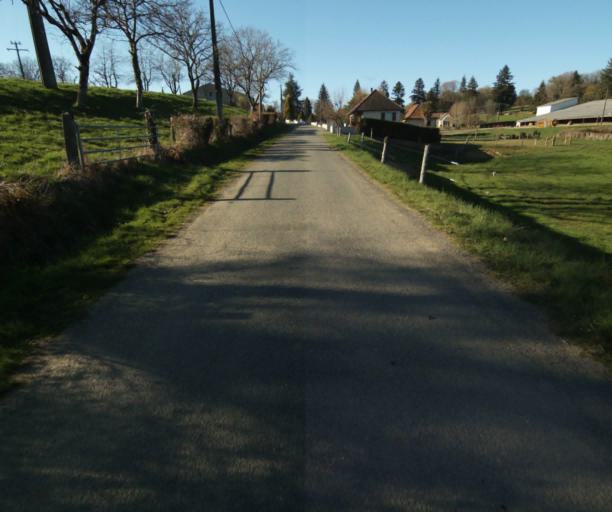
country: FR
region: Limousin
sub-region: Departement de la Correze
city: Seilhac
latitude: 45.3773
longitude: 1.7159
